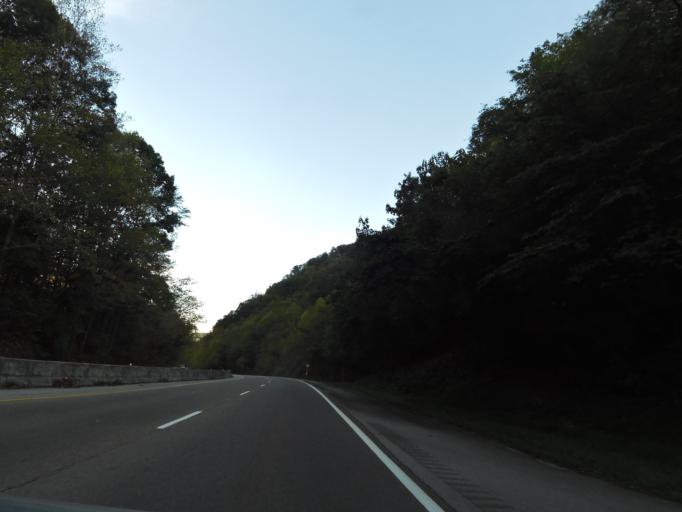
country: US
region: Tennessee
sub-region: Blount County
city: Wildwood
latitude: 35.7361
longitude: -83.8239
